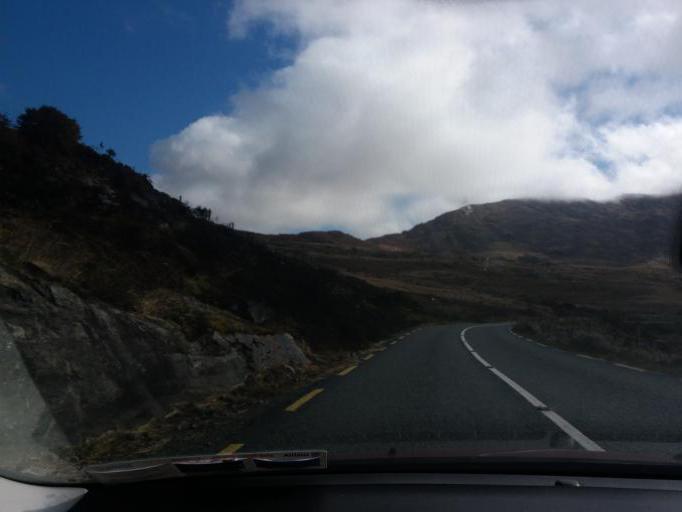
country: IE
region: Munster
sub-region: Ciarrai
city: Kenmare
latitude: 51.9273
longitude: -9.6454
